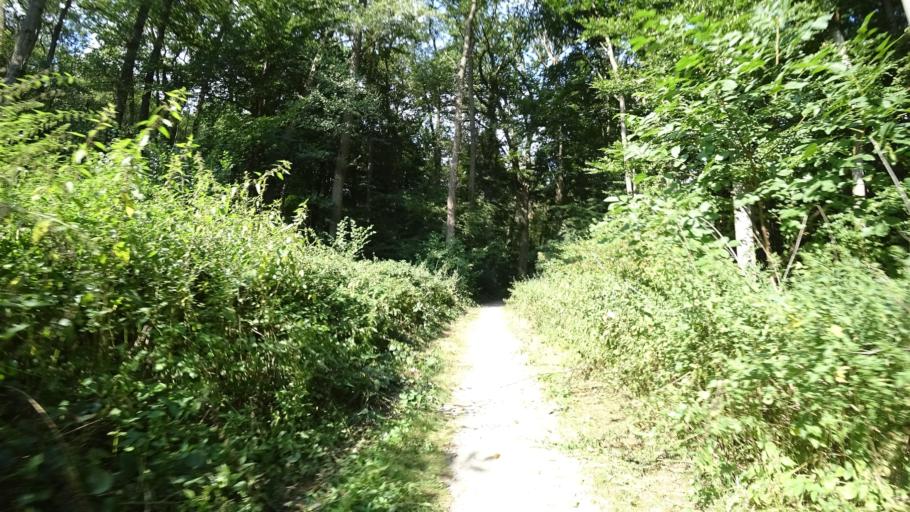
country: DE
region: North Rhine-Westphalia
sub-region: Regierungsbezirk Detmold
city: Rheda-Wiedenbruck
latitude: 51.8264
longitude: 8.2719
